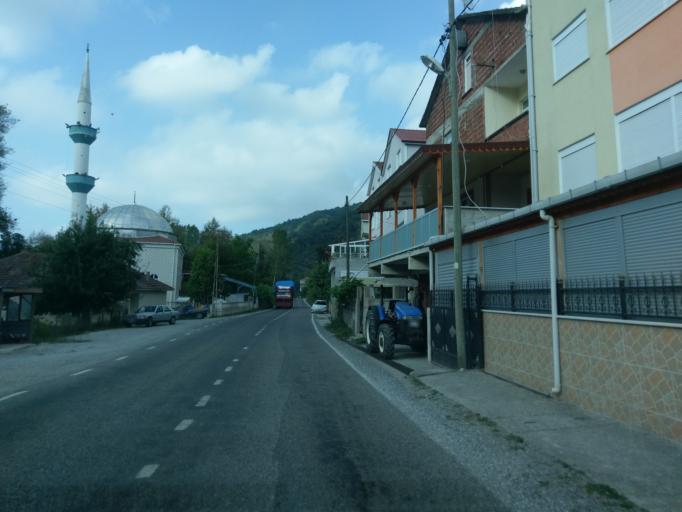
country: TR
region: Sinop
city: Helaldi
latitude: 41.9245
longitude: 34.4152
